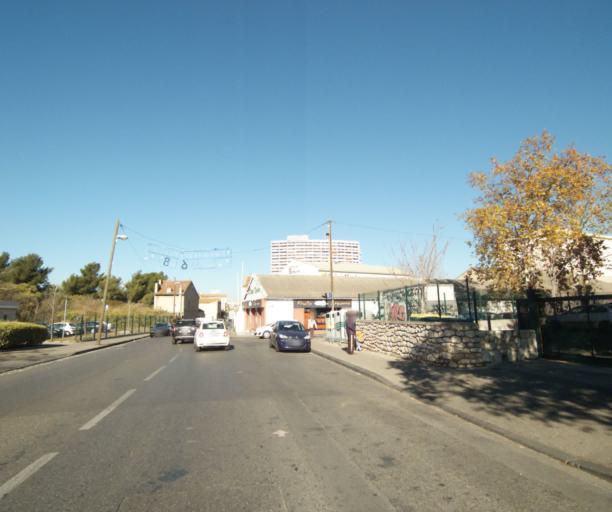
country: FR
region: Provence-Alpes-Cote d'Azur
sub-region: Departement des Bouches-du-Rhone
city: Marseille 09
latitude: 43.2612
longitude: 5.3937
